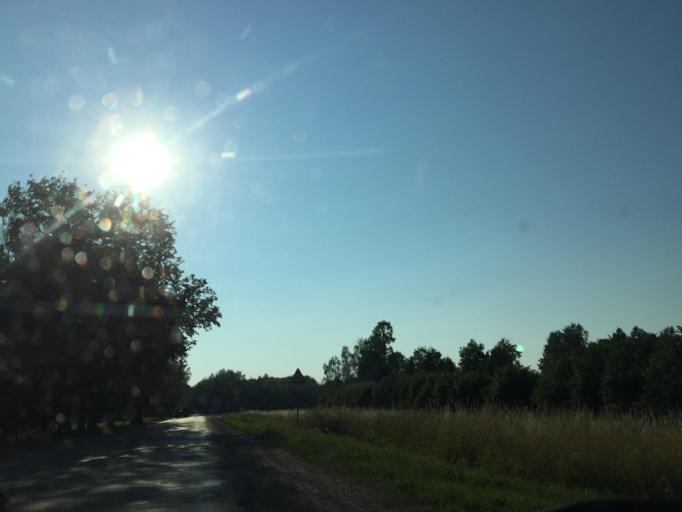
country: LV
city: Tervete
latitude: 56.4219
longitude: 23.5509
